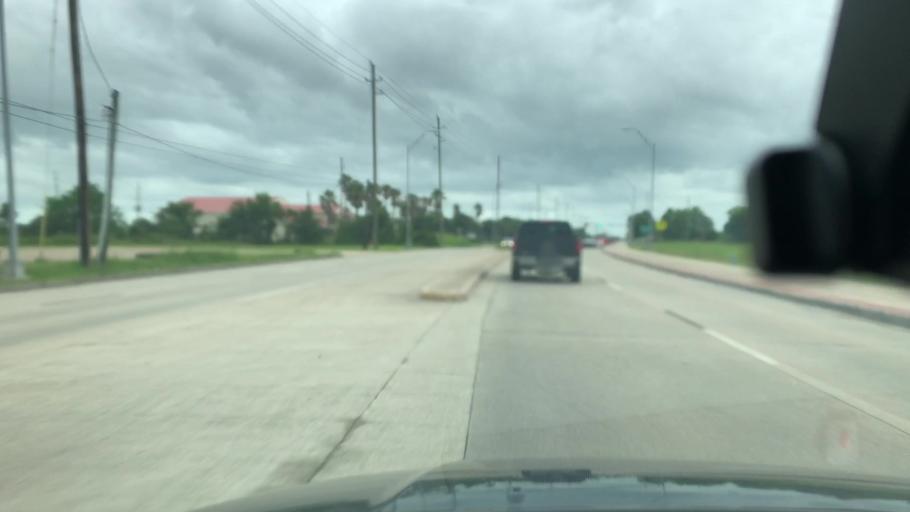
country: US
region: Texas
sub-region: Brazoria County
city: Brookside Village
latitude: 29.5788
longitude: -95.3510
